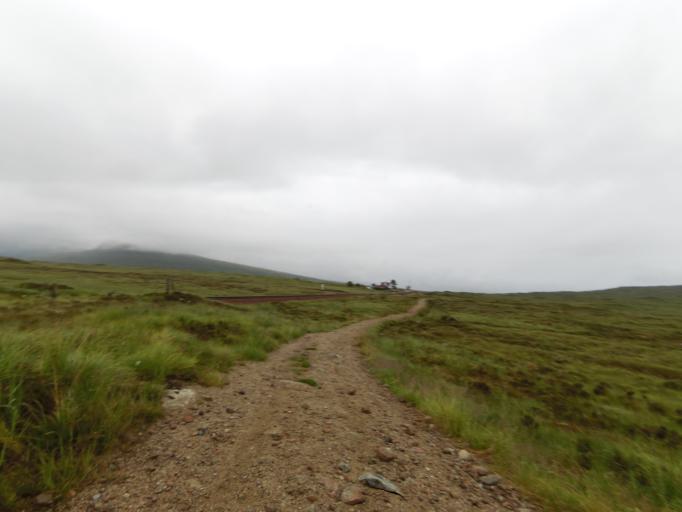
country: GB
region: Scotland
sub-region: Highland
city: Spean Bridge
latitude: 56.7626
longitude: -4.6952
